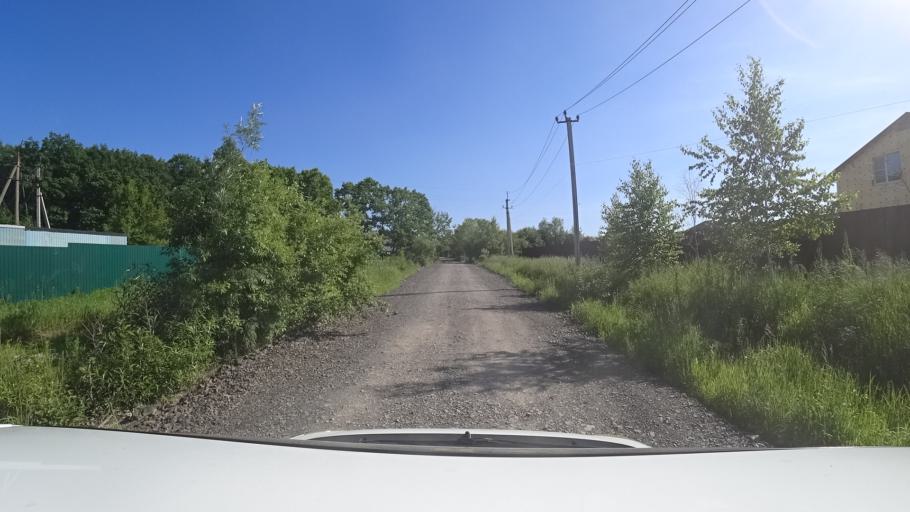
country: RU
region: Khabarovsk Krai
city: Topolevo
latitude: 48.5491
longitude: 135.1828
